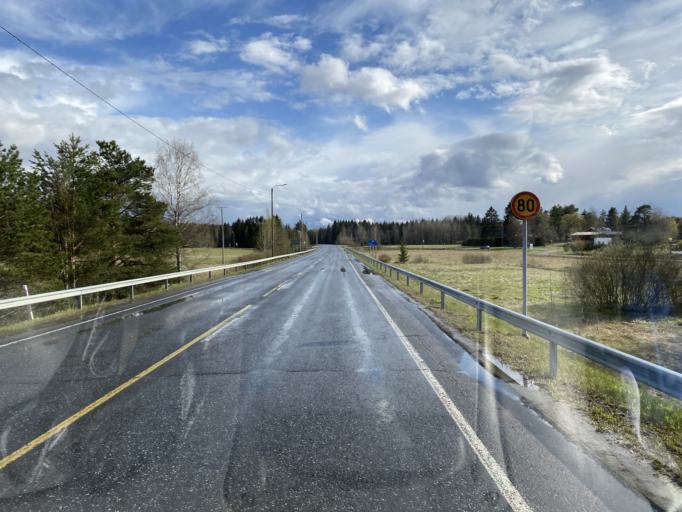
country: FI
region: Pirkanmaa
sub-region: Etelae-Pirkanmaa
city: Viiala
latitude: 61.2219
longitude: 23.7383
